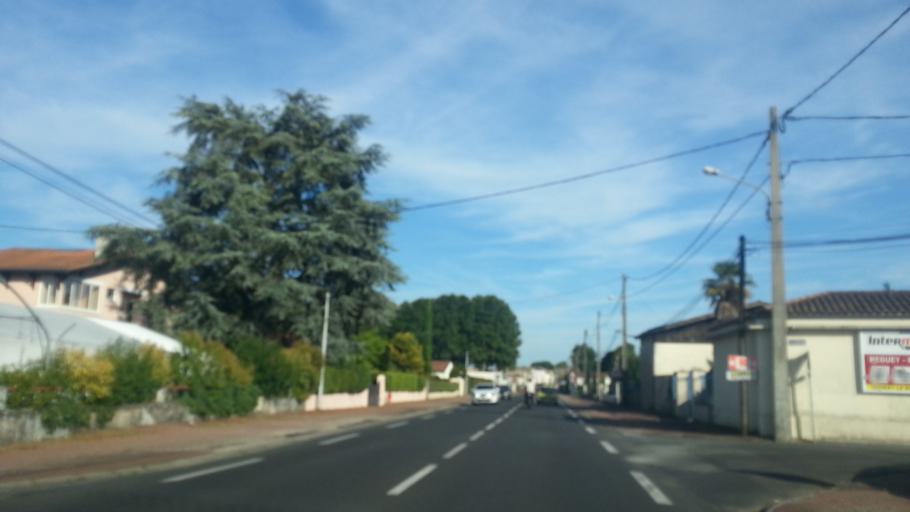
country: FR
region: Aquitaine
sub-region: Departement de la Gironde
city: Podensac
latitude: 44.6538
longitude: -0.3609
